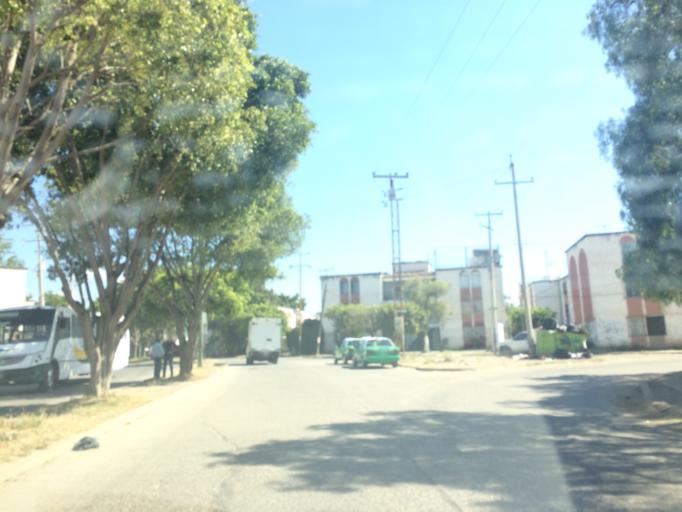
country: MX
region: Guanajuato
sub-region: Leon
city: San Jose de Duran (Los Troncoso)
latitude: 21.0959
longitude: -101.6710
